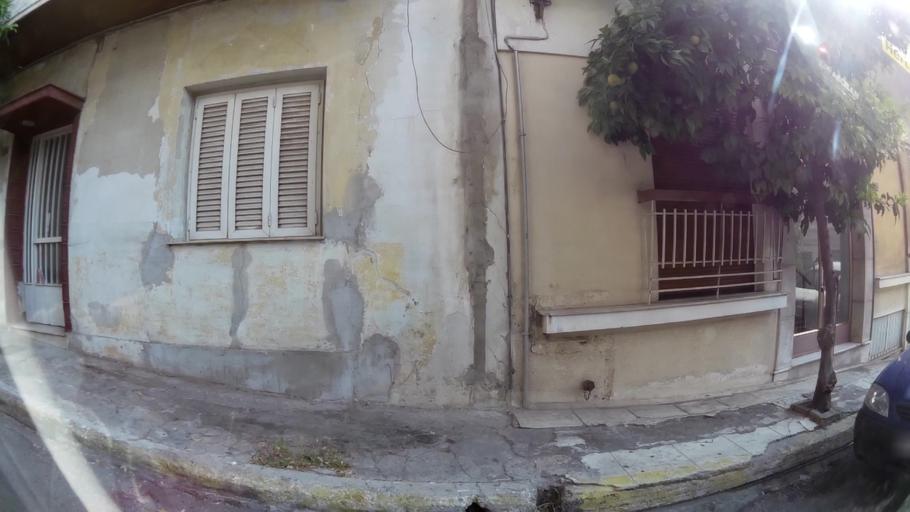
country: GR
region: Attica
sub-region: Nomos Piraios
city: Keratsini
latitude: 37.9635
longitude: 23.6298
